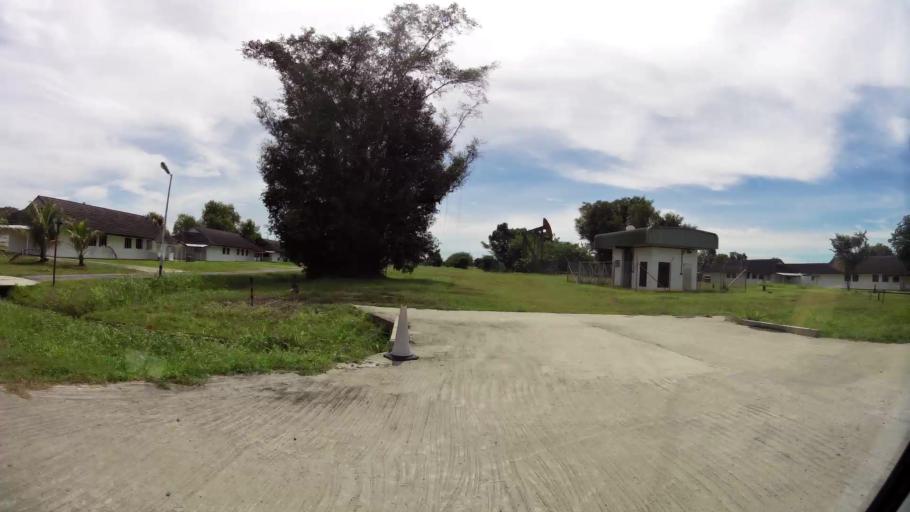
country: BN
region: Belait
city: Seria
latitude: 4.6082
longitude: 114.3160
